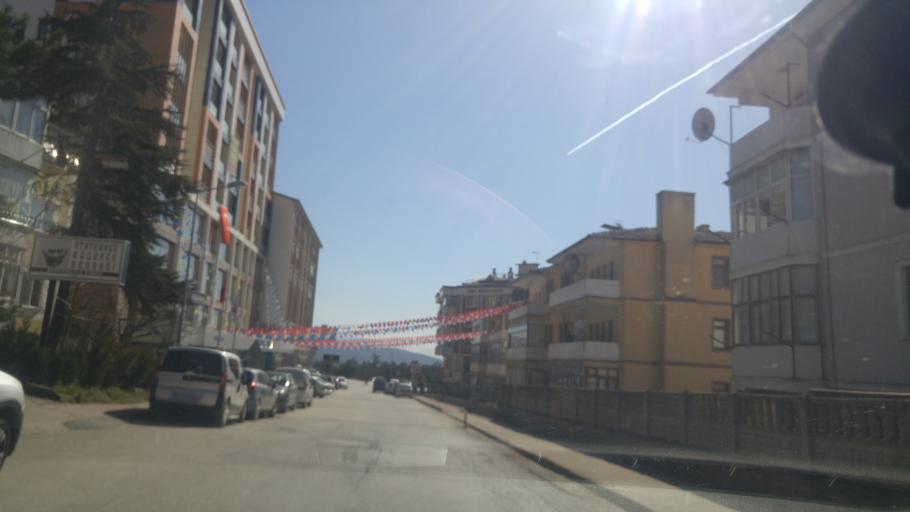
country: TR
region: Karabuk
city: Safranbolu
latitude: 41.2487
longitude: 32.6812
